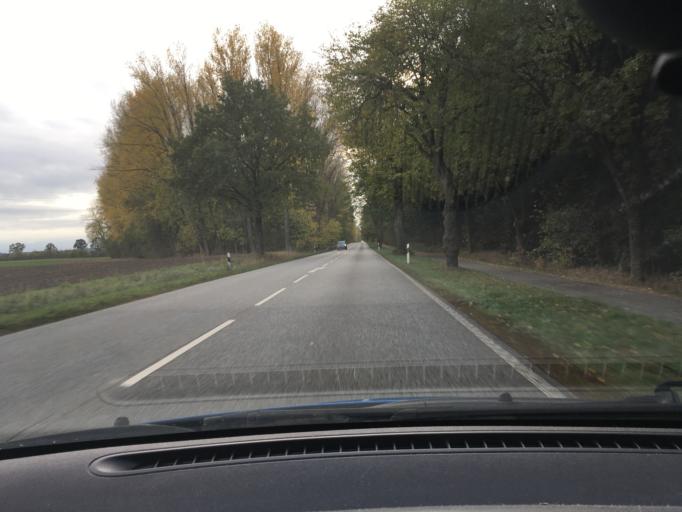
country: DE
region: Schleswig-Holstein
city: Sahms
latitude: 53.5362
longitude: 10.5262
